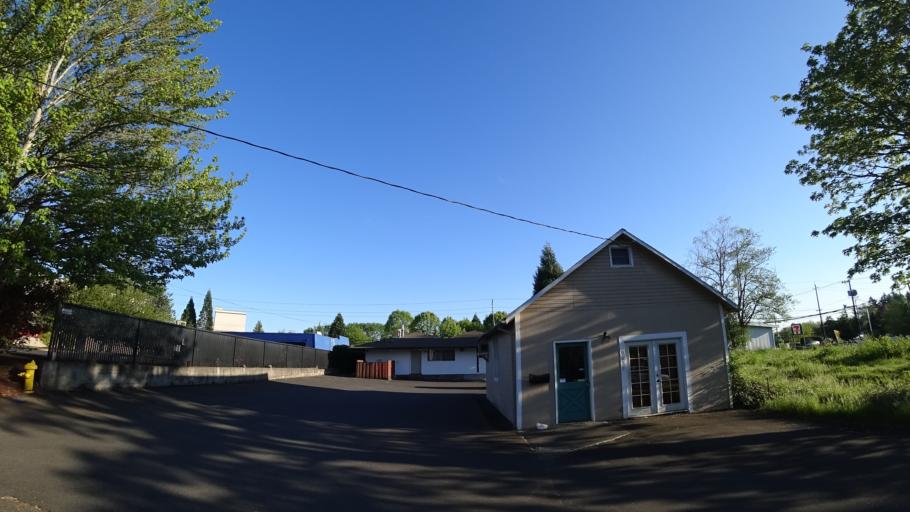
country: US
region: Oregon
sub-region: Washington County
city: Raleigh Hills
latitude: 45.4872
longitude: -122.7701
